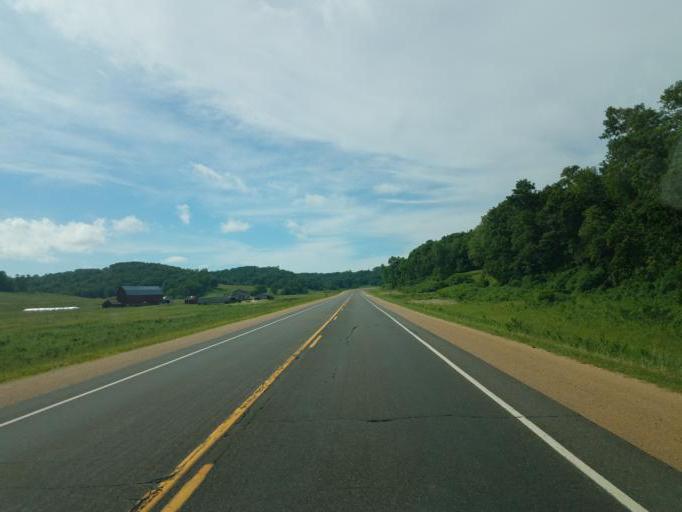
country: US
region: Wisconsin
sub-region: Monroe County
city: Tomah
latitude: 43.8725
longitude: -90.4769
